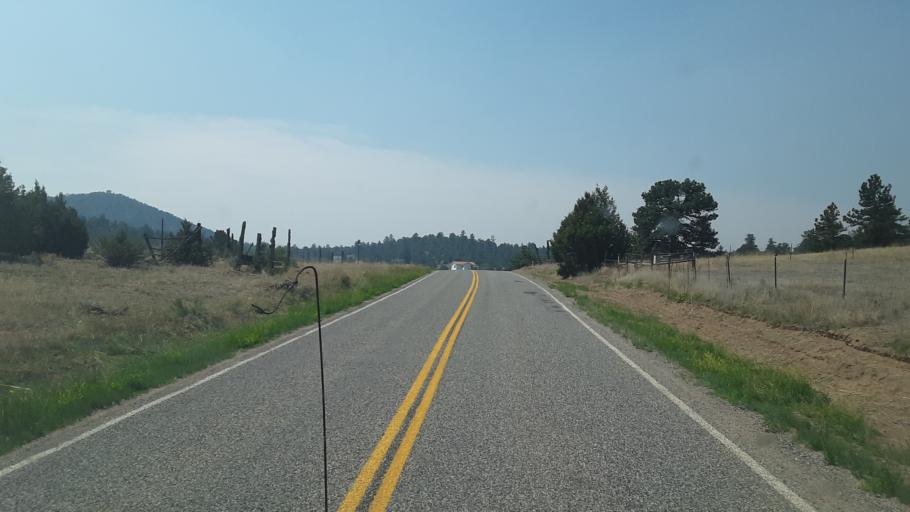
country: US
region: Colorado
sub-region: Fremont County
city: Canon City
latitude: 38.3755
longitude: -105.4564
